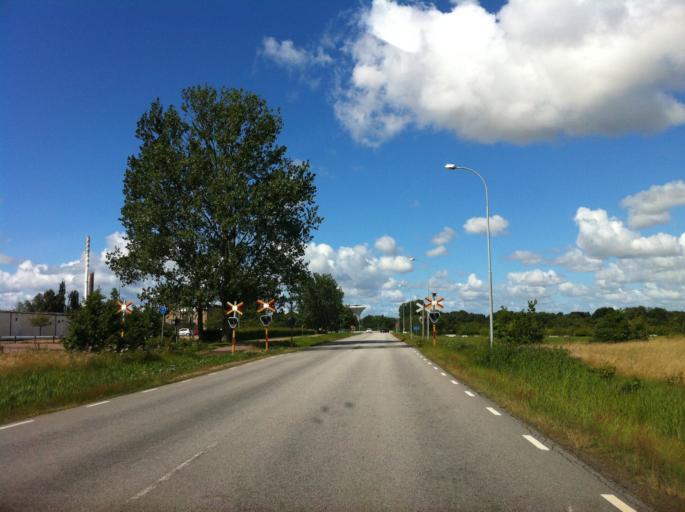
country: SE
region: Skane
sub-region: Bjuvs Kommun
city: Billesholm
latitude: 56.0619
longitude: 13.0509
